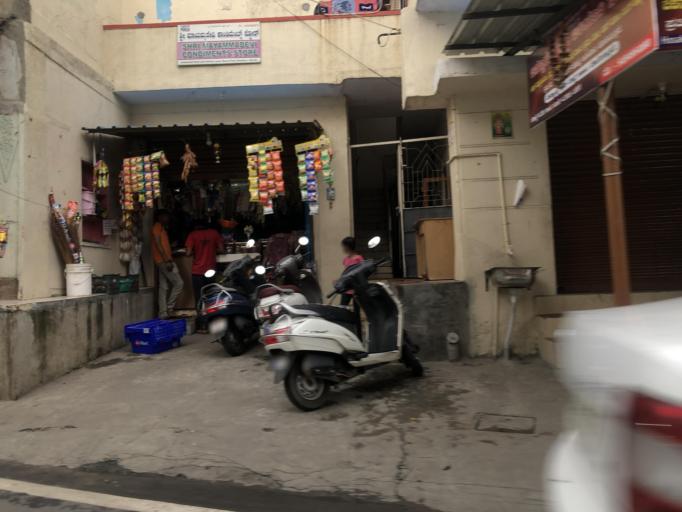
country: IN
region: Karnataka
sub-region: Bangalore Urban
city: Bangalore
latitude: 12.9503
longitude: 77.5389
